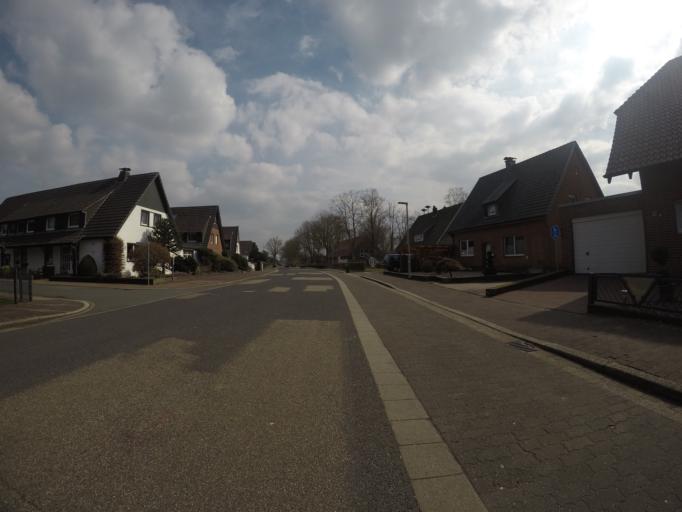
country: DE
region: North Rhine-Westphalia
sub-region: Regierungsbezirk Munster
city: Isselburg
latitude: 51.8203
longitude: 6.5123
